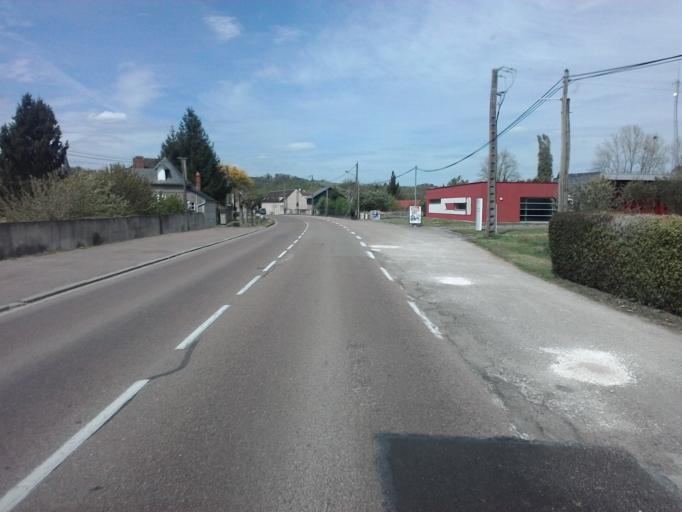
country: FR
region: Bourgogne
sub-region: Departement de l'Yonne
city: Vermenton
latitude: 47.6605
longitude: 3.7365
